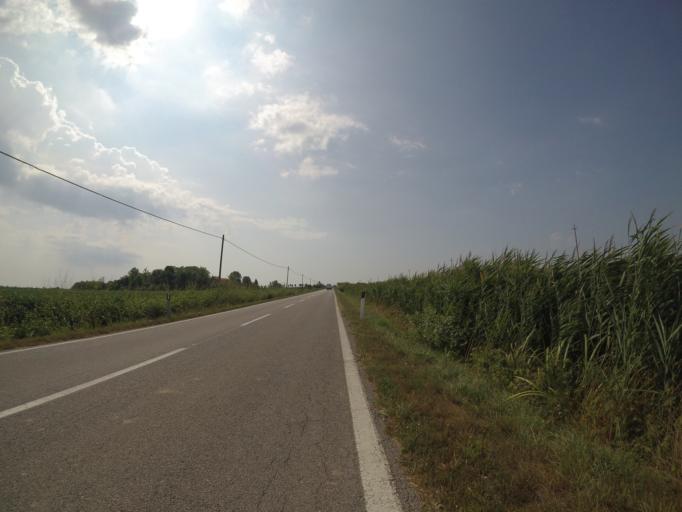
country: IT
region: Friuli Venezia Giulia
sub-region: Provincia di Udine
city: Pertegada
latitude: 45.7463
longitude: 13.0611
